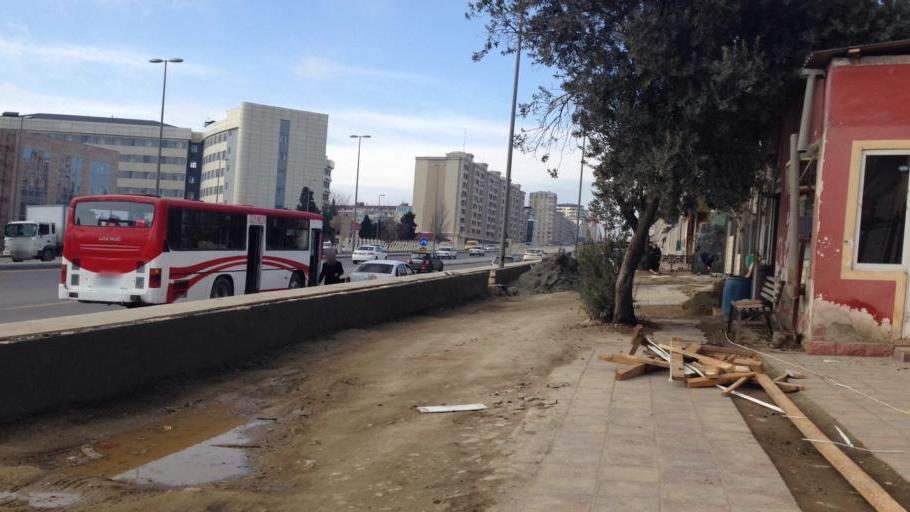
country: AZ
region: Baki
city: Baku
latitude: 40.4147
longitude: 49.8524
